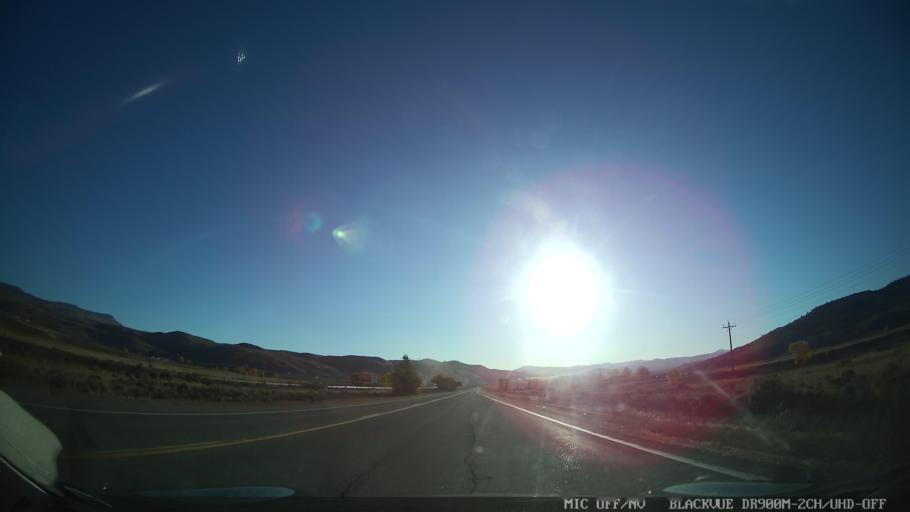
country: US
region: Colorado
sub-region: Grand County
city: Hot Sulphur Springs
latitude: 40.0673
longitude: -106.2178
